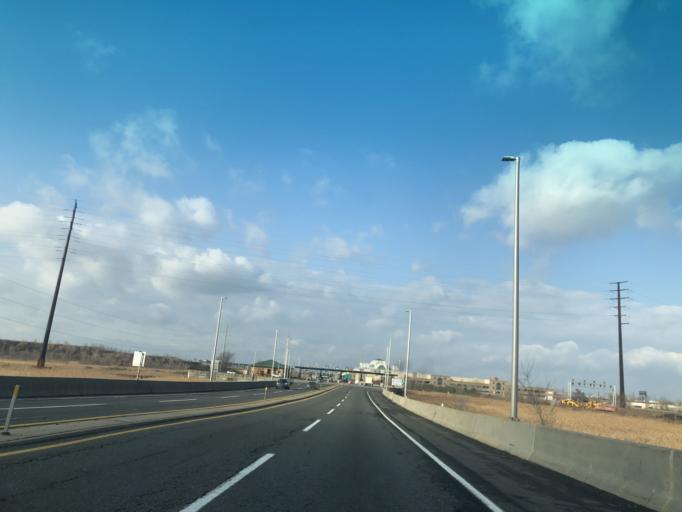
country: US
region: New Jersey
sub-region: Hudson County
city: Jersey City
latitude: 40.7544
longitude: -74.0723
